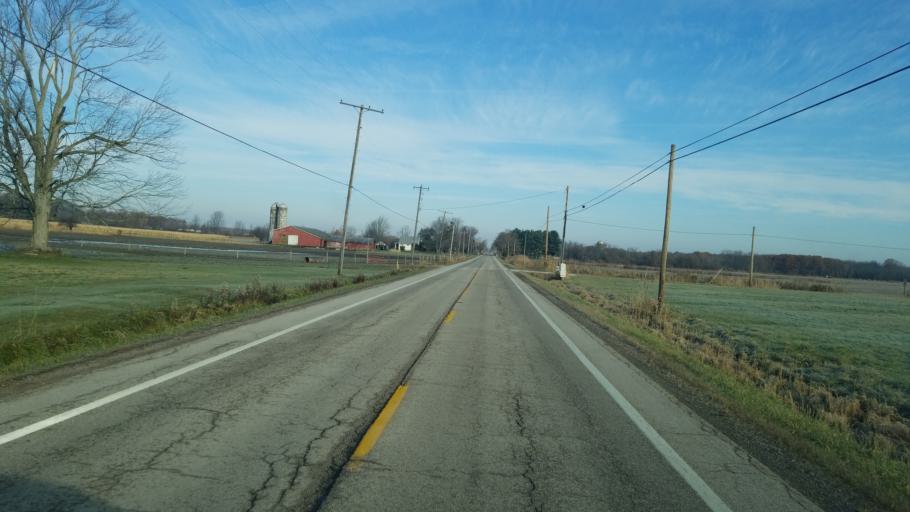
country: US
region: Ohio
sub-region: Ashtabula County
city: Jefferson
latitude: 41.7650
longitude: -80.6680
